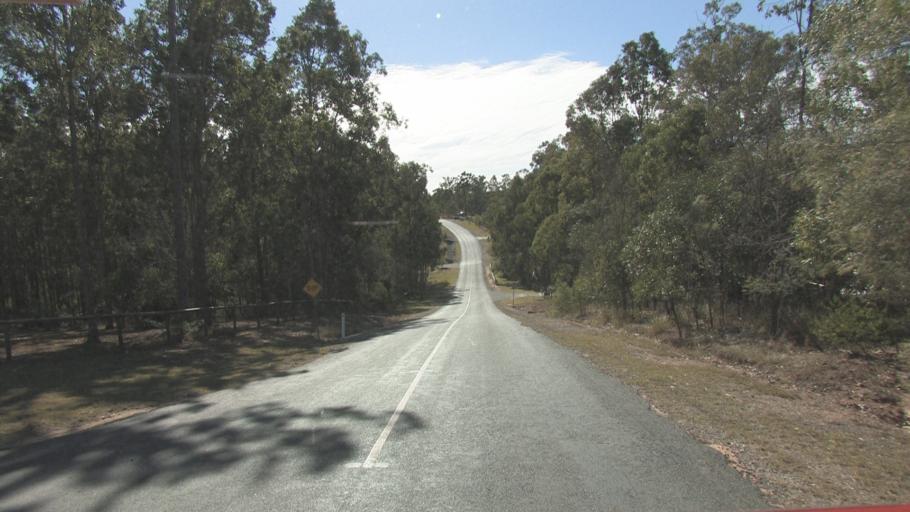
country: AU
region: Queensland
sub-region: Ipswich
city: Springfield Lakes
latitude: -27.7182
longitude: 152.9147
